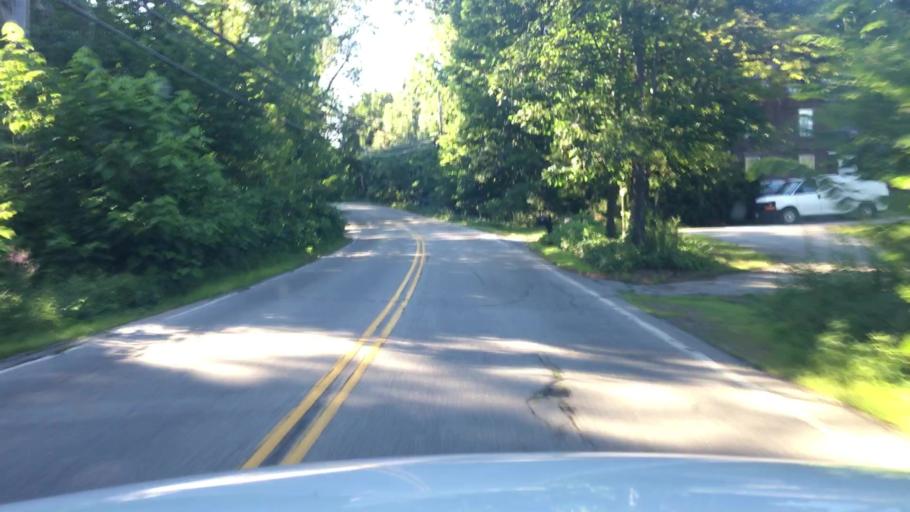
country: US
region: New Hampshire
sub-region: Rockingham County
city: Sandown
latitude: 42.9127
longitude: -71.1622
